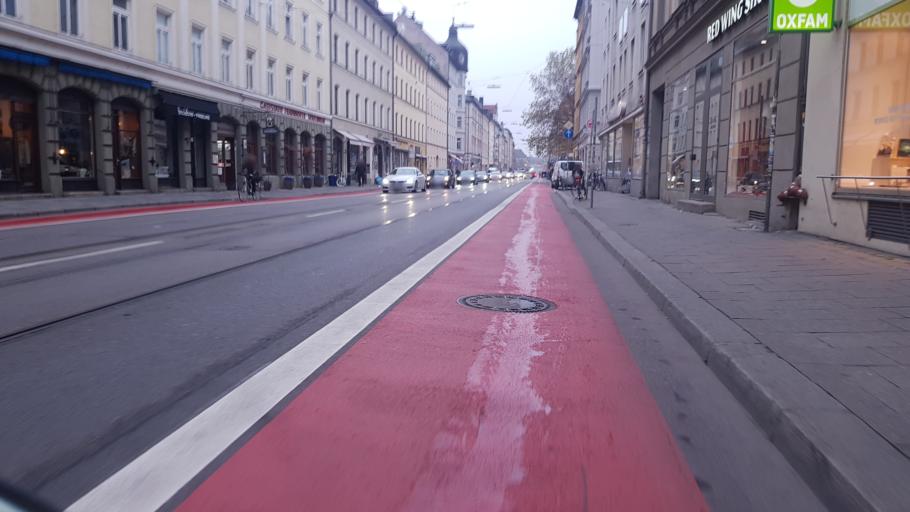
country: DE
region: Bavaria
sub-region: Upper Bavaria
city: Munich
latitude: 48.1309
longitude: 11.5720
